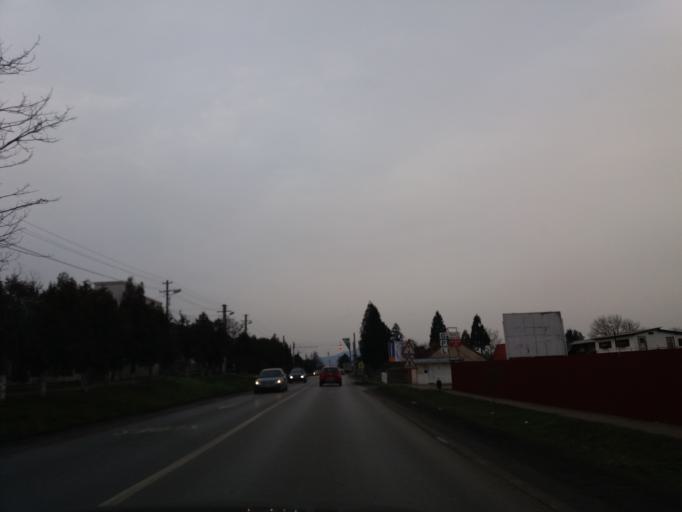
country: RO
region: Hunedoara
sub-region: Oras Simeria
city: Simeria
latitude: 45.8446
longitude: 23.0104
